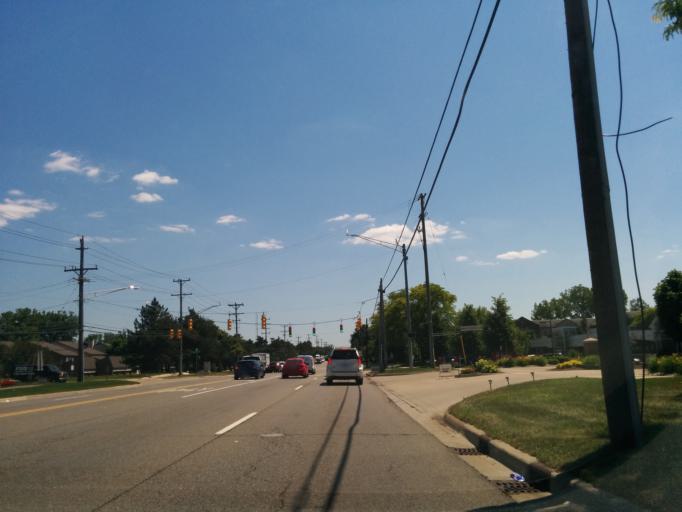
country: US
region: Michigan
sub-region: Oakland County
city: Orchard Lake
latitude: 42.5740
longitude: -83.3622
